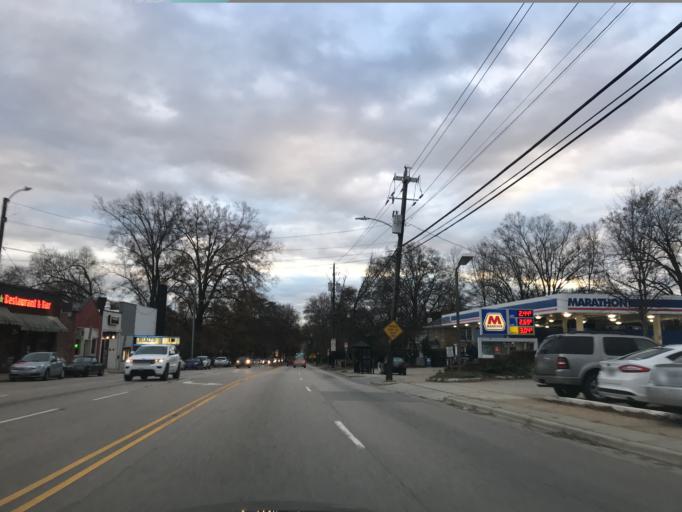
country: US
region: North Carolina
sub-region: Wake County
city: West Raleigh
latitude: 35.8037
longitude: -78.6459
